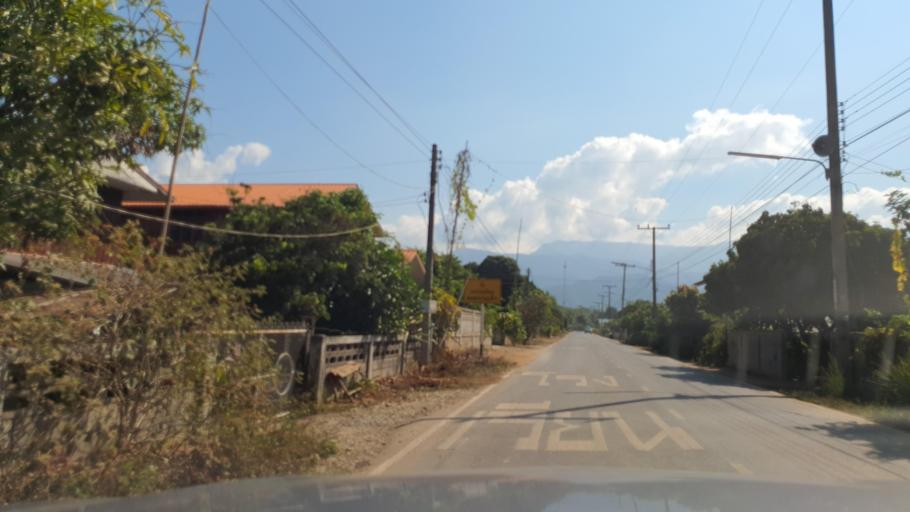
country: TH
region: Nan
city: Pua
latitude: 19.1450
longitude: 100.9220
